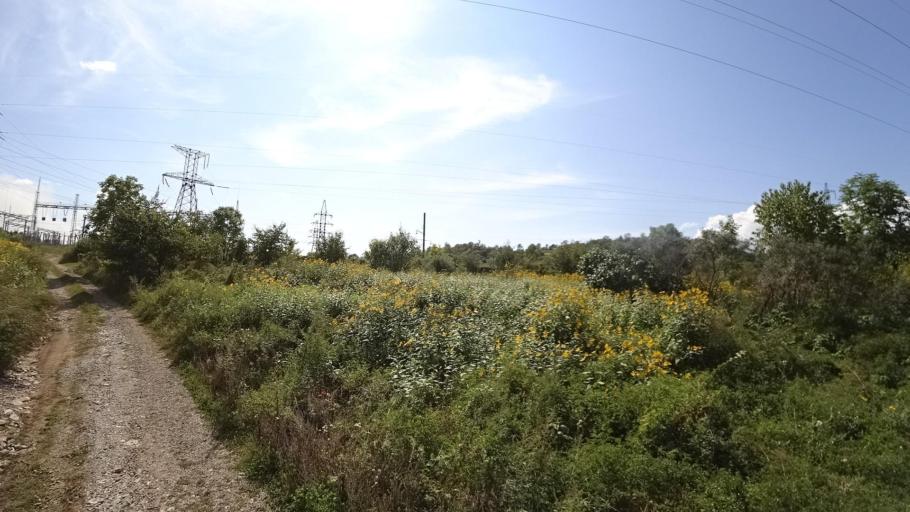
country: RU
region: Jewish Autonomous Oblast
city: Londoko
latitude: 49.0158
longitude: 131.8961
